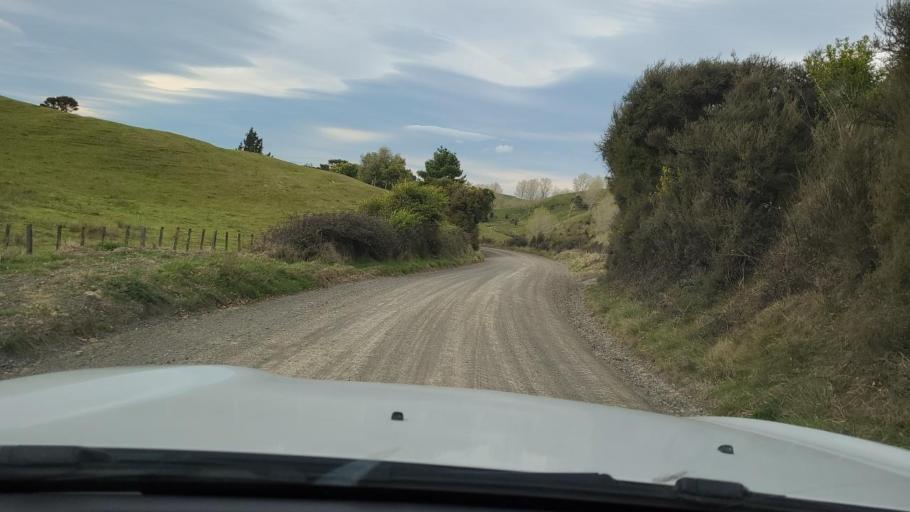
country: NZ
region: Hawke's Bay
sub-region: Napier City
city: Napier
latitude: -39.3045
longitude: 176.8239
